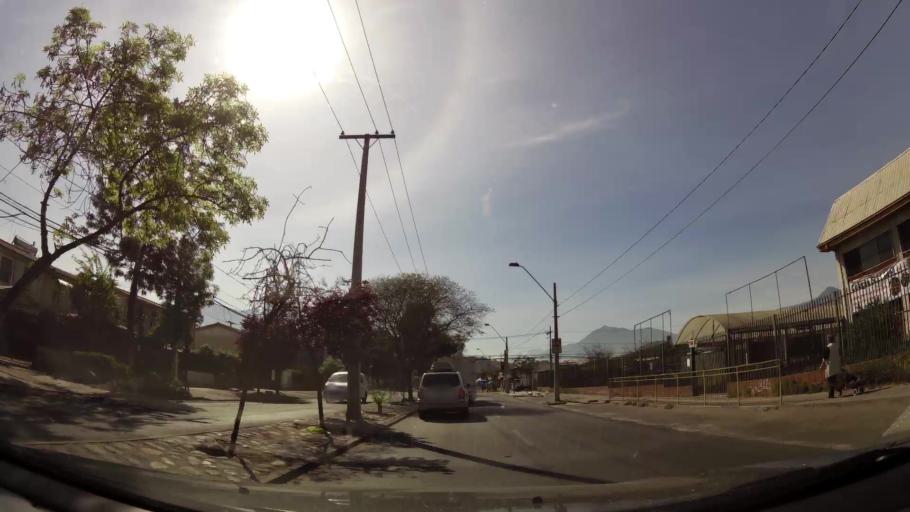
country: CL
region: Santiago Metropolitan
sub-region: Provincia de Cordillera
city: Puente Alto
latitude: -33.6015
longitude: -70.5661
